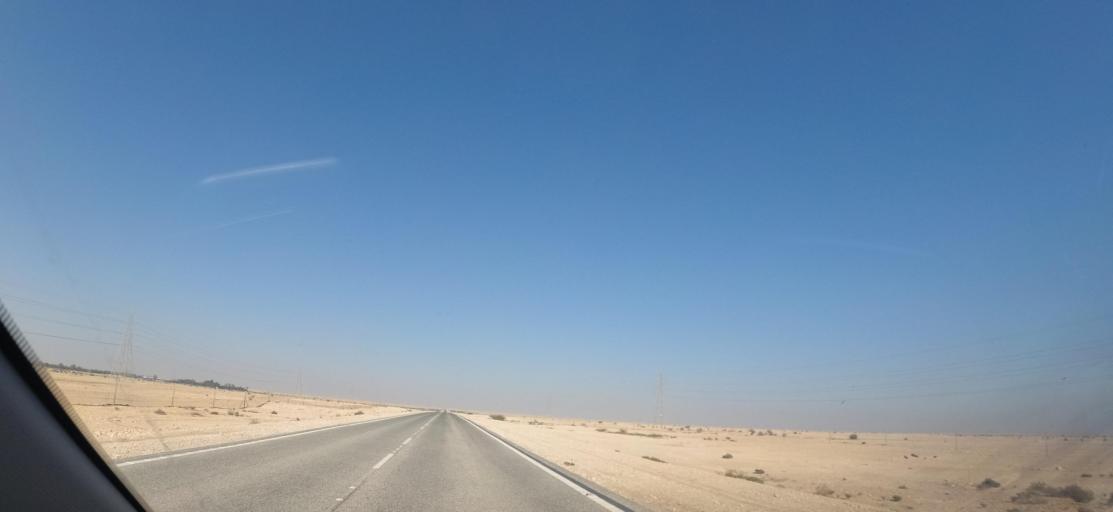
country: QA
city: Al Jumayliyah
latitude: 25.6614
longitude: 51.1205
